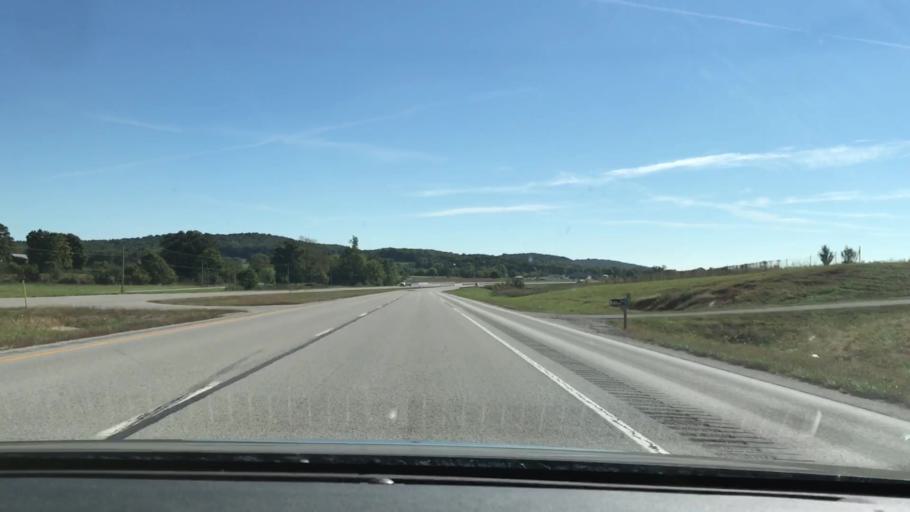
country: US
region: Kentucky
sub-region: Todd County
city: Elkton
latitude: 36.8401
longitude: -87.2505
